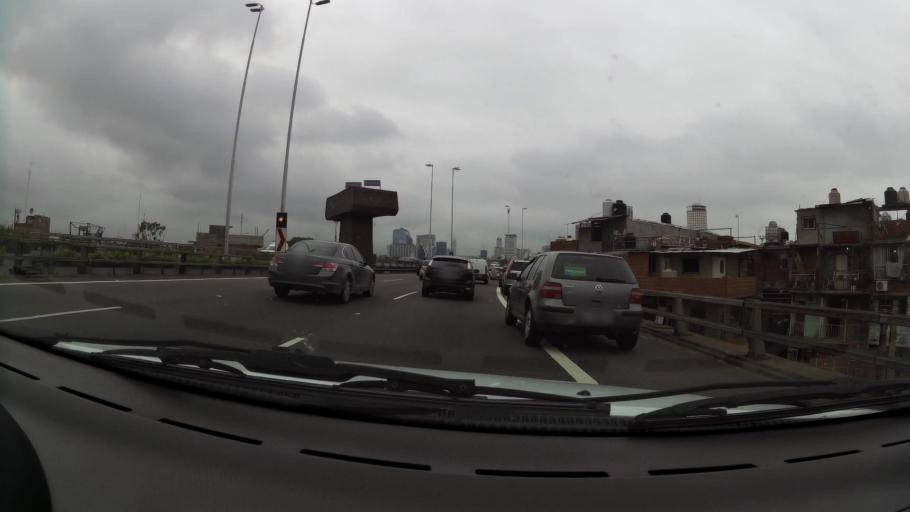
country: AR
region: Buenos Aires F.D.
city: Retiro
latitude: -34.5838
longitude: -58.3803
